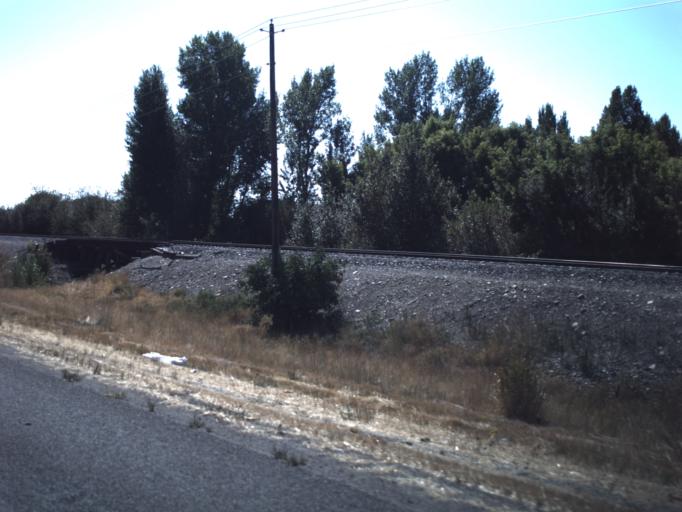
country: US
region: Utah
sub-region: Cache County
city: Richmond
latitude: 41.9576
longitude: -111.8130
